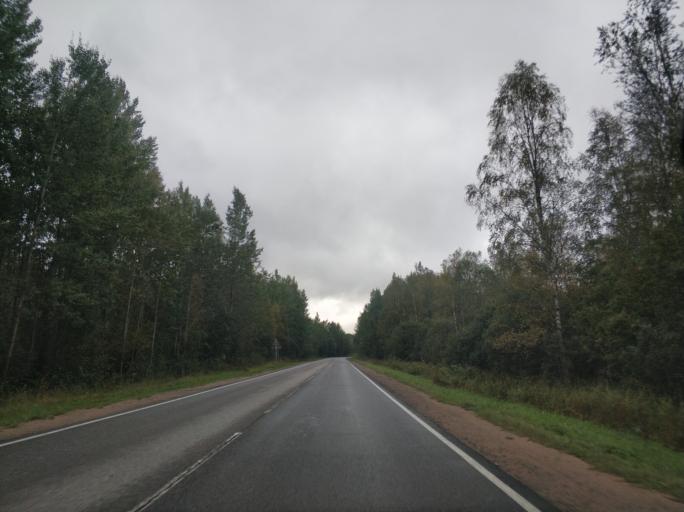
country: RU
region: Leningrad
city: Borisova Griva
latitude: 60.1178
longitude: 30.9637
